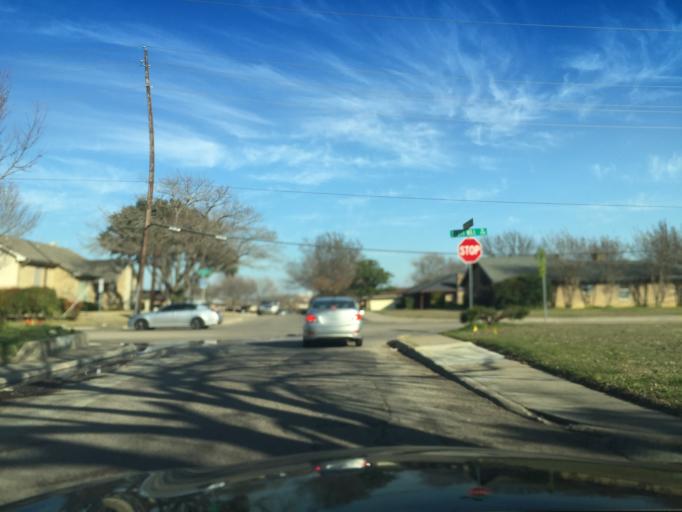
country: US
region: Texas
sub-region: Dallas County
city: Carrollton
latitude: 32.9846
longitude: -96.8844
